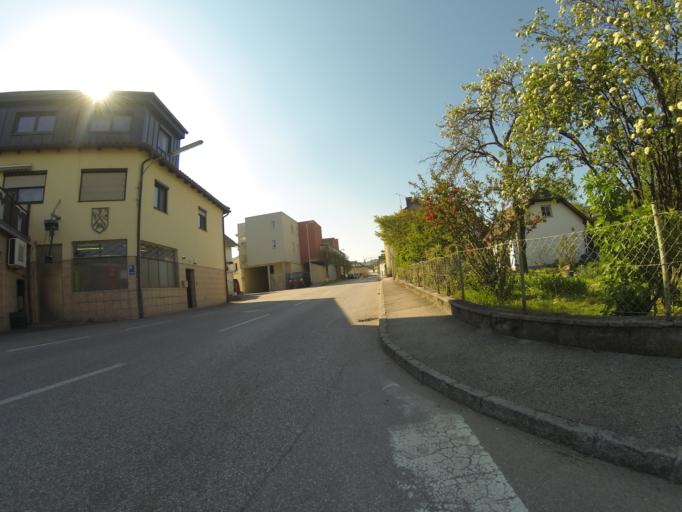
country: AT
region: Upper Austria
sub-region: Politischer Bezirk Gmunden
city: Altmunster
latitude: 47.9295
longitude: 13.7722
